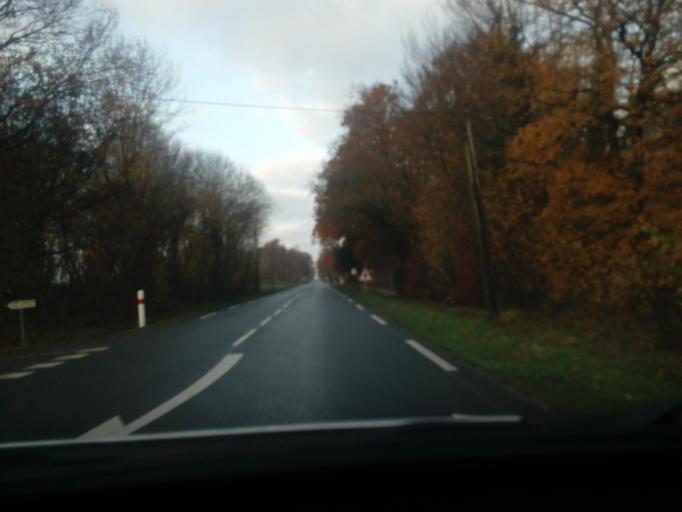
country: FR
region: Poitou-Charentes
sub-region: Departement de la Charente-Maritime
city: Jonzac
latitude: 45.4427
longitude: -0.3559
